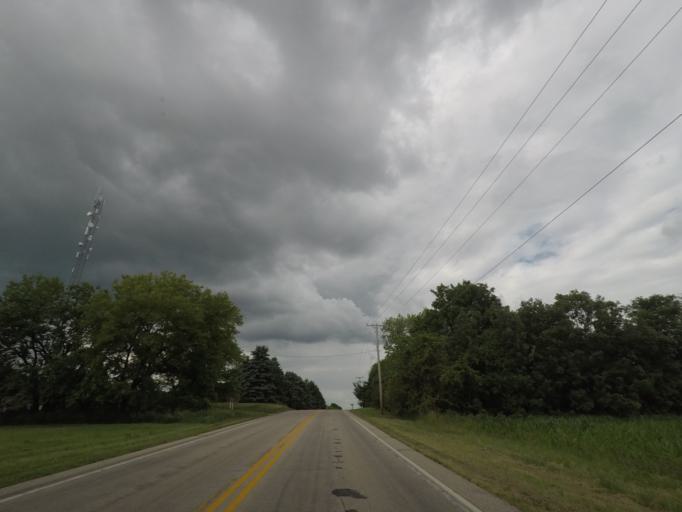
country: US
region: Wisconsin
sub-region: Green County
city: Brooklyn
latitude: 42.8351
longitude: -89.4125
